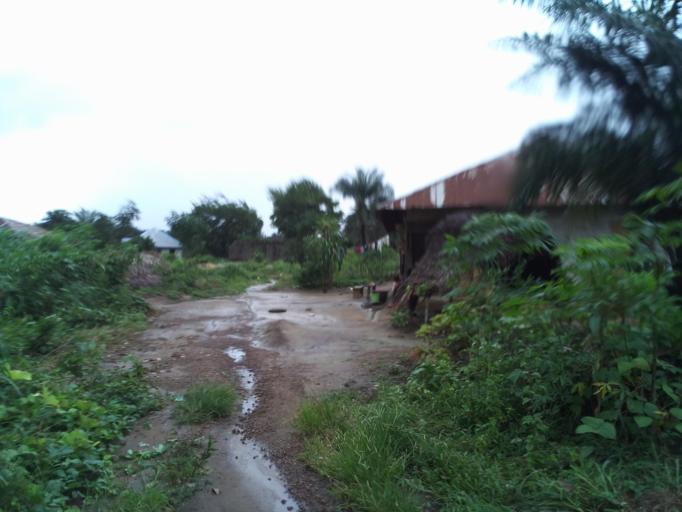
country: SL
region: Eastern Province
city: Kenema
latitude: 7.8779
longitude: -11.1557
